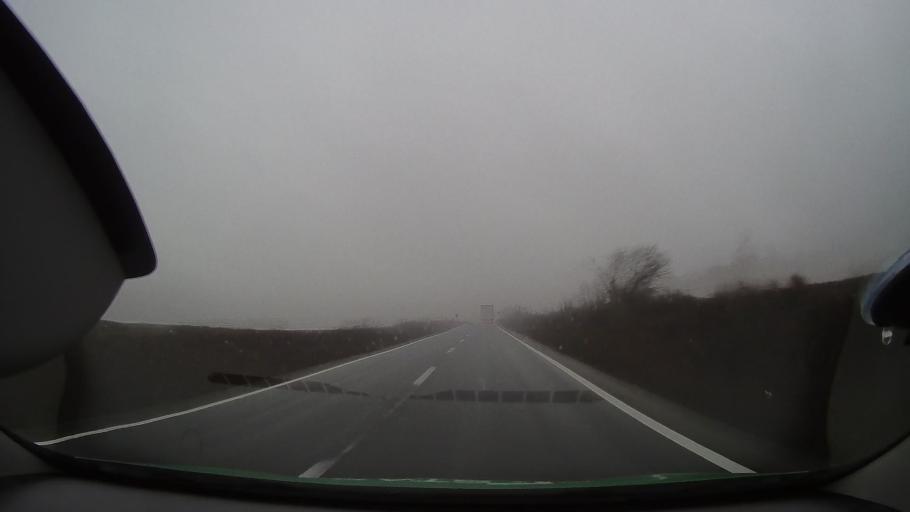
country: RO
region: Bihor
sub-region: Comuna Olcea
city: Olcea
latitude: 46.6775
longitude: 21.9656
